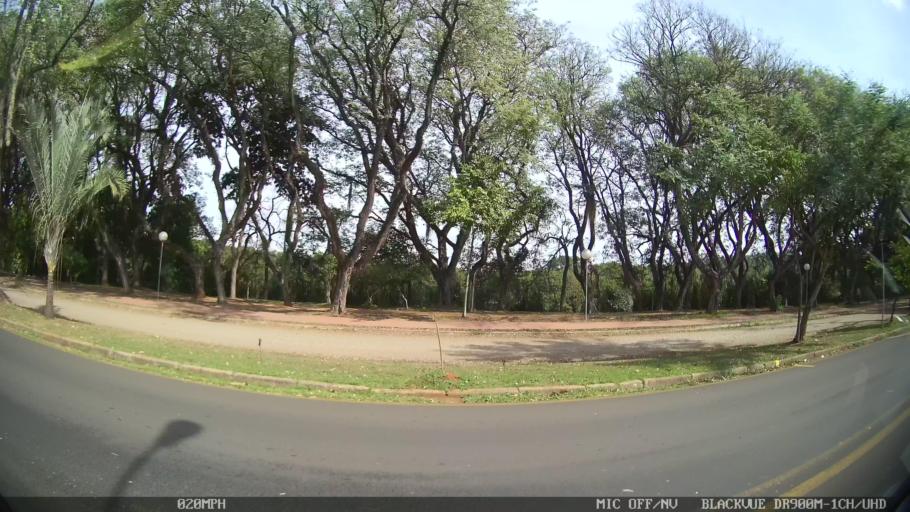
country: BR
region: Sao Paulo
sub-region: Piracicaba
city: Piracicaba
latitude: -22.7214
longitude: -47.6716
